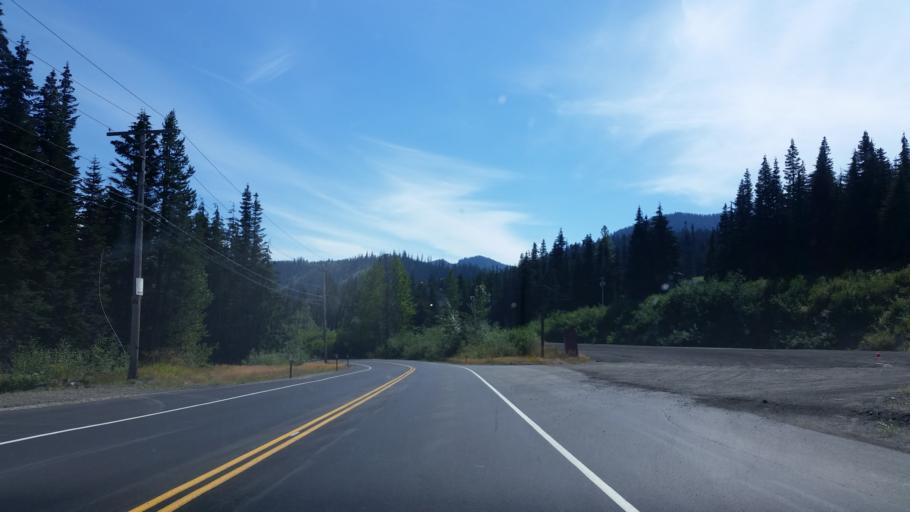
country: US
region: Washington
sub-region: King County
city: Tanner
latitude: 47.4065
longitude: -121.4117
